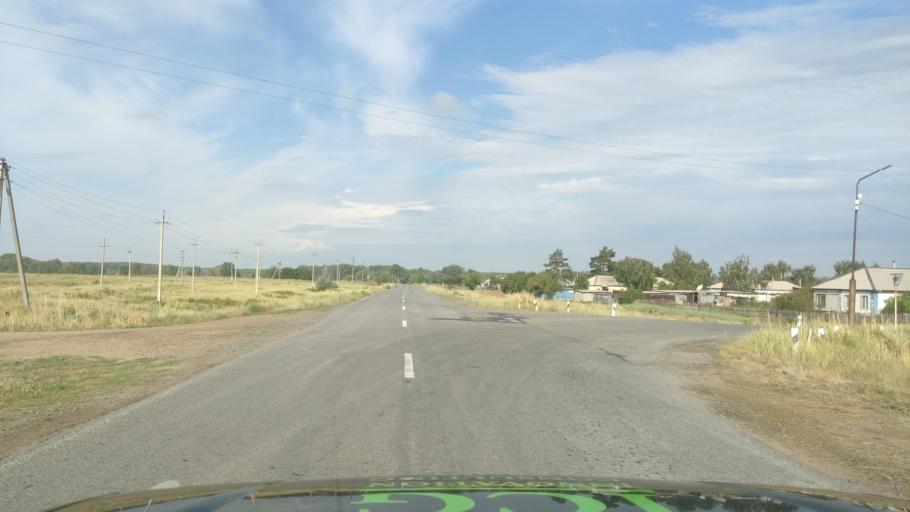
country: KZ
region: Pavlodar
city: Leninskiy
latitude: 52.4775
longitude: 76.8218
